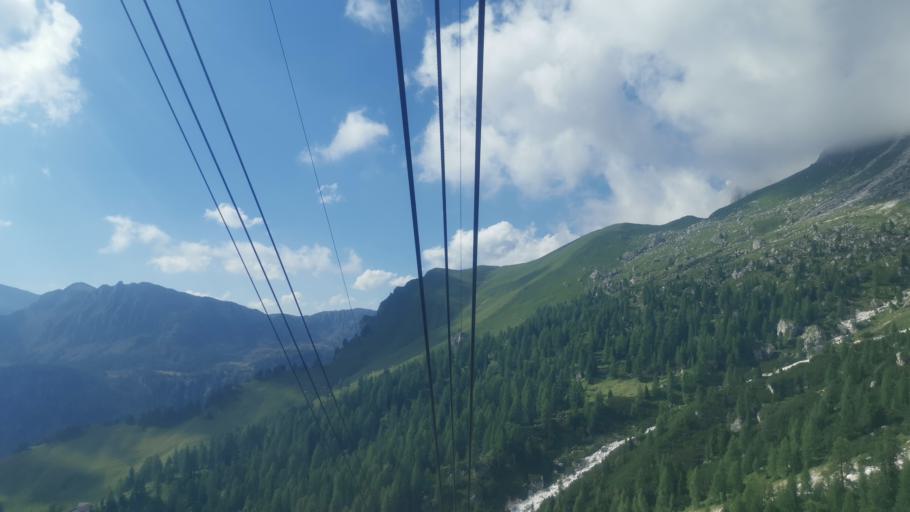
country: IT
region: Trentino-Alto Adige
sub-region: Provincia di Trento
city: Siror
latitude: 46.2709
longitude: 11.8232
